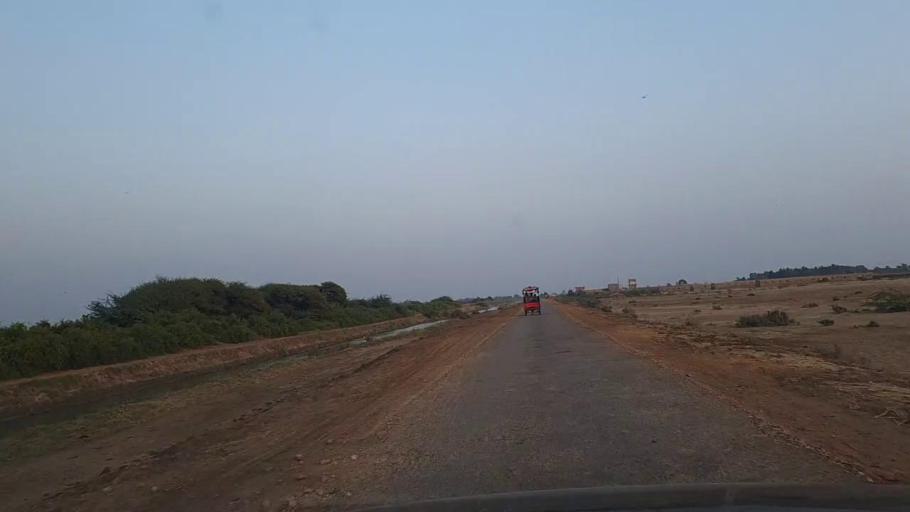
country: PK
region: Sindh
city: Mirpur Sakro
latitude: 24.6357
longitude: 67.6055
